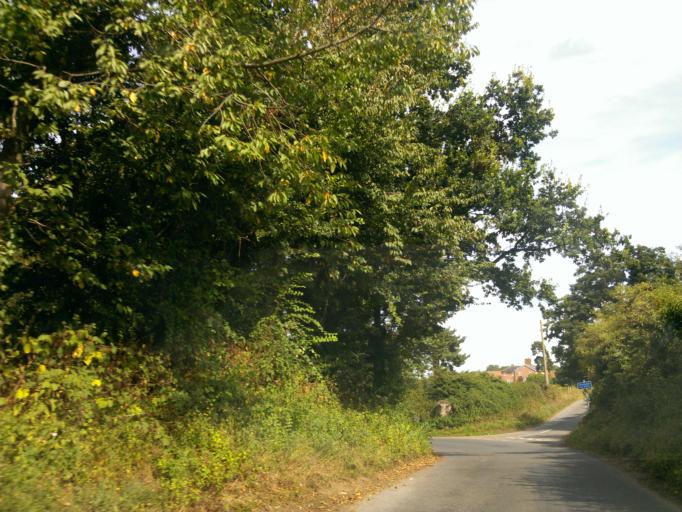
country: GB
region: England
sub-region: Essex
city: Sible Hedingham
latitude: 51.9604
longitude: 0.6310
